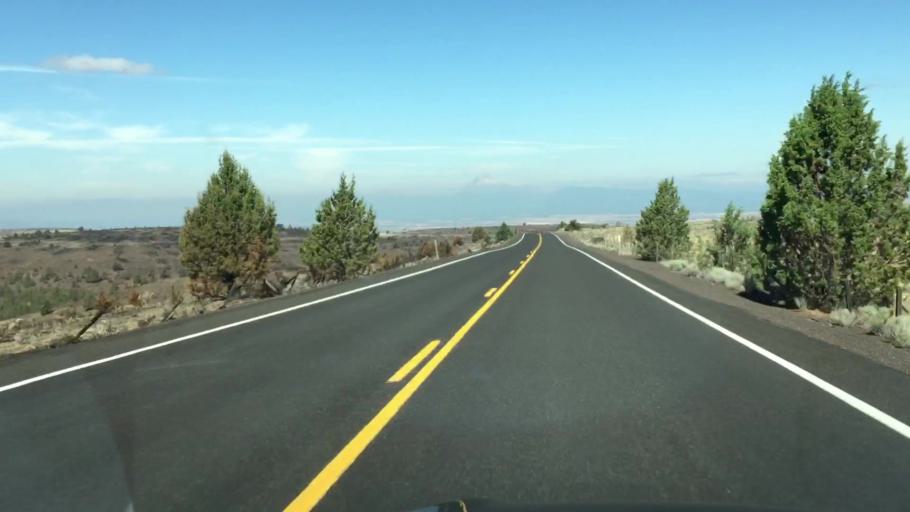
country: US
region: Oregon
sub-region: Jefferson County
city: Warm Springs
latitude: 45.0554
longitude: -121.0218
